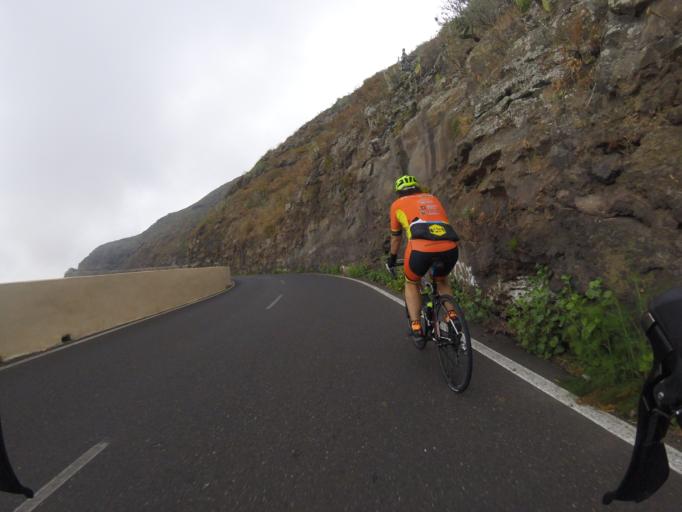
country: ES
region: Canary Islands
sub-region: Provincia de Santa Cruz de Tenerife
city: Guimar
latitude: 28.2942
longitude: -16.4088
